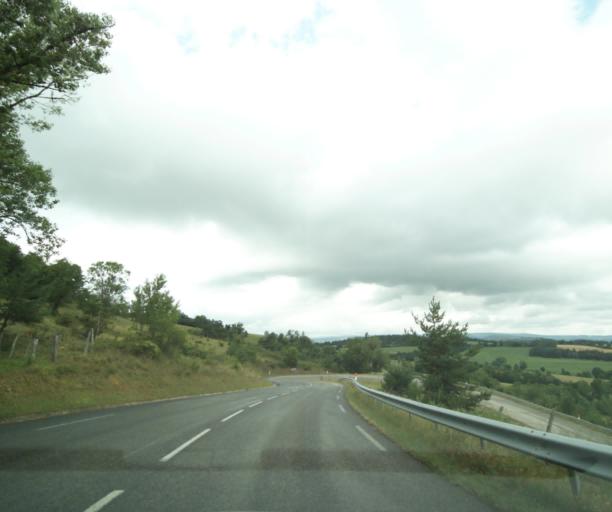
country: FR
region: Languedoc-Roussillon
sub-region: Departement de la Lozere
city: La Canourgue
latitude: 44.4210
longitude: 3.1808
